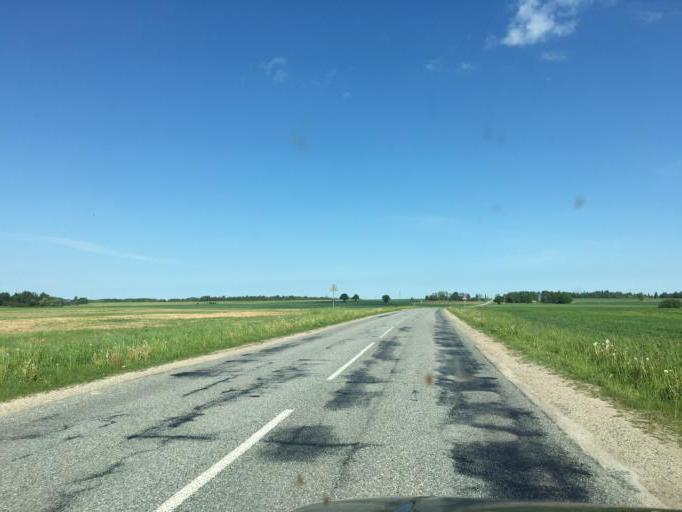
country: LV
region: Talsu Rajons
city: Valdemarpils
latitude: 57.3467
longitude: 22.5003
